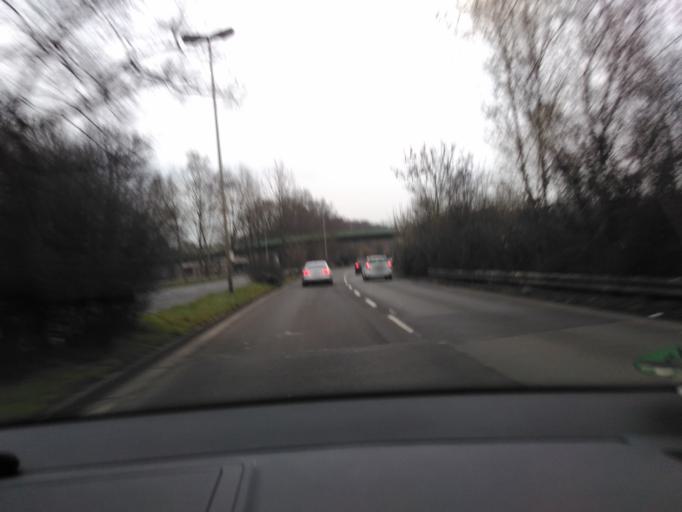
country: DE
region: North Rhine-Westphalia
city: Opladen
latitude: 51.0367
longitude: 7.0365
